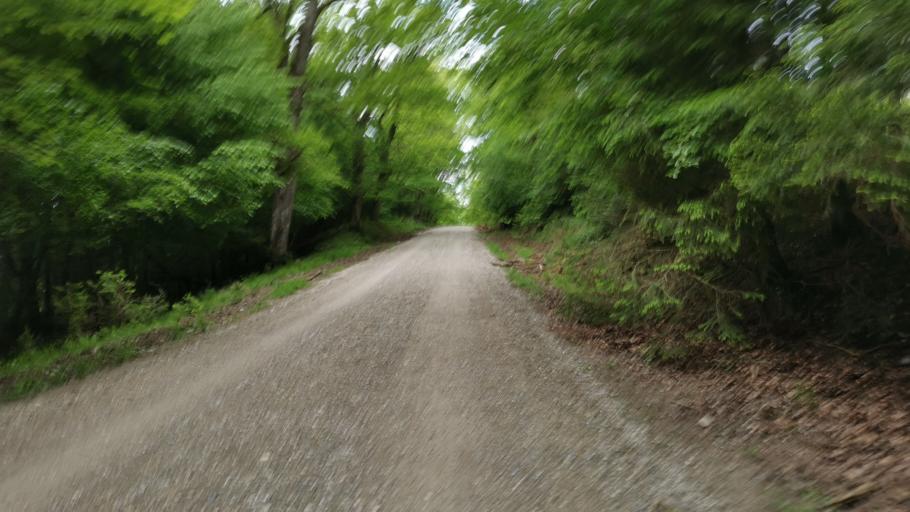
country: DE
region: Bavaria
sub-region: Upper Bavaria
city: Baierbrunn
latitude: 48.0442
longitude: 11.4708
